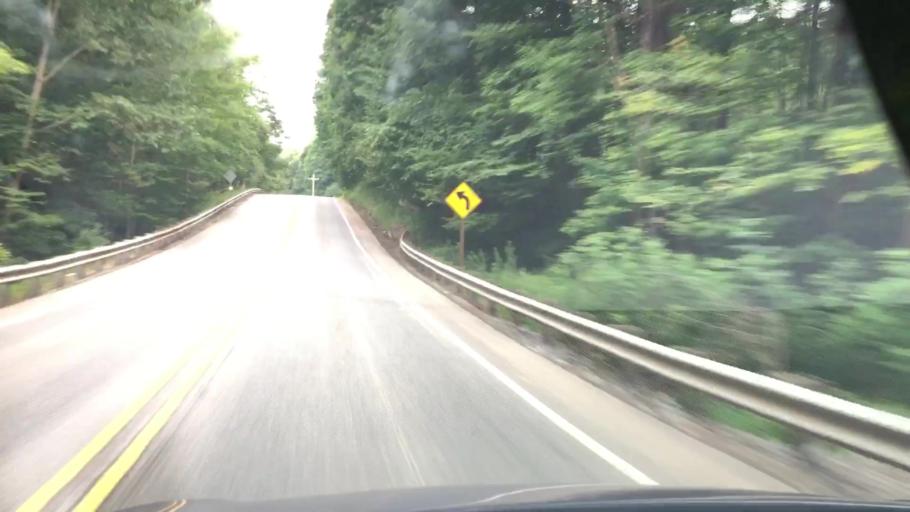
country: US
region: Pennsylvania
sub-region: Venango County
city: Hasson Heights
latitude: 41.5178
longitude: -79.7065
